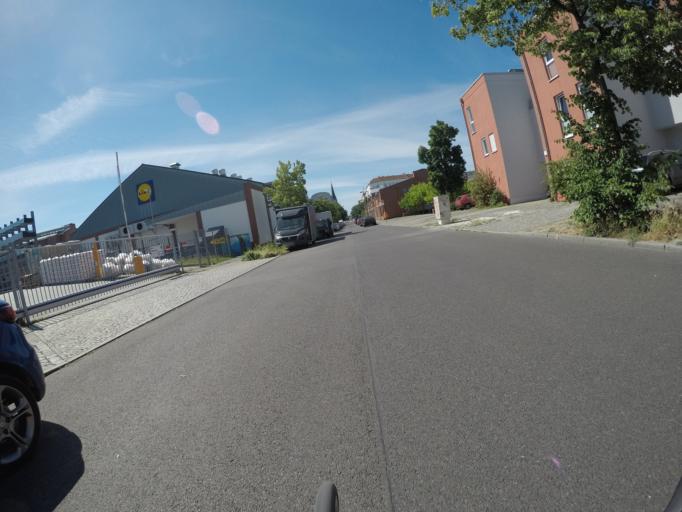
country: DE
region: Berlin
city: Fennpfuhl
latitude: 52.5213
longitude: 13.4674
